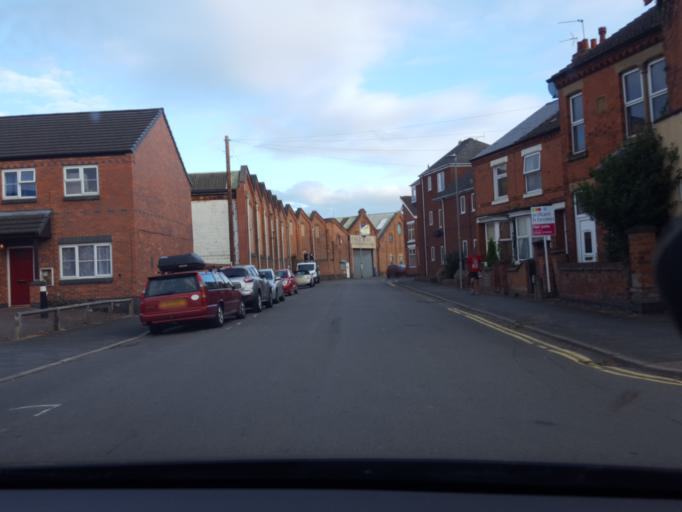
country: GB
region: England
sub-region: Leicestershire
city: Loughborough
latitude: 52.7709
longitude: -1.1925
